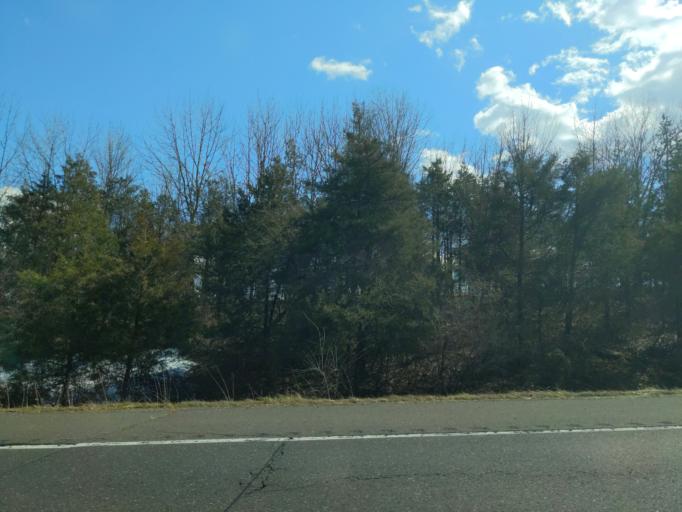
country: US
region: Pennsylvania
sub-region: Bucks County
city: Spinnerstown
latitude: 40.4229
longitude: -75.4433
